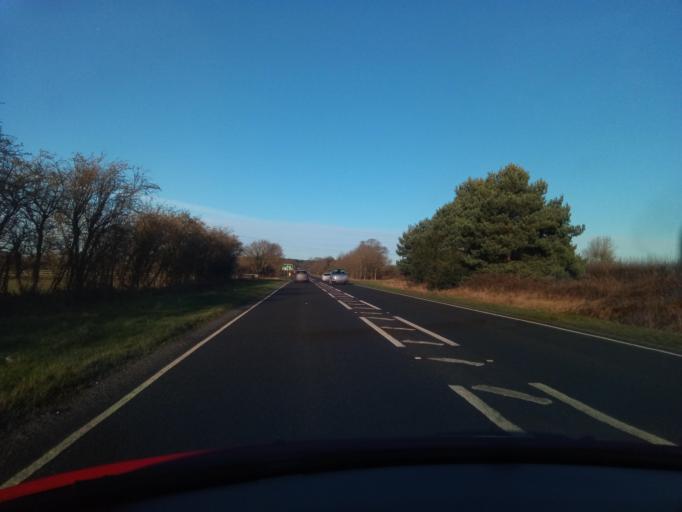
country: GB
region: England
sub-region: Nottinghamshire
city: Farnsfield
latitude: 53.0473
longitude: -1.0634
